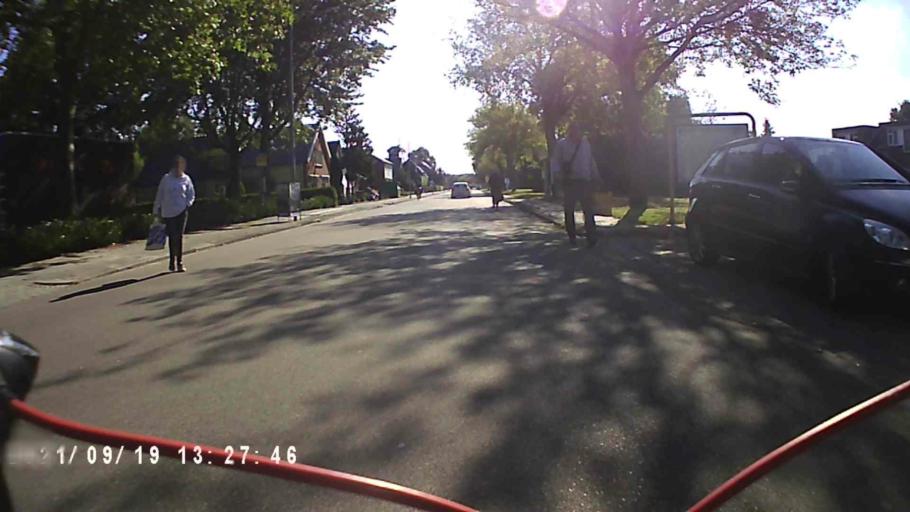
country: NL
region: Groningen
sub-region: Gemeente  Oldambt
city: Winschoten
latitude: 53.1503
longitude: 7.0215
